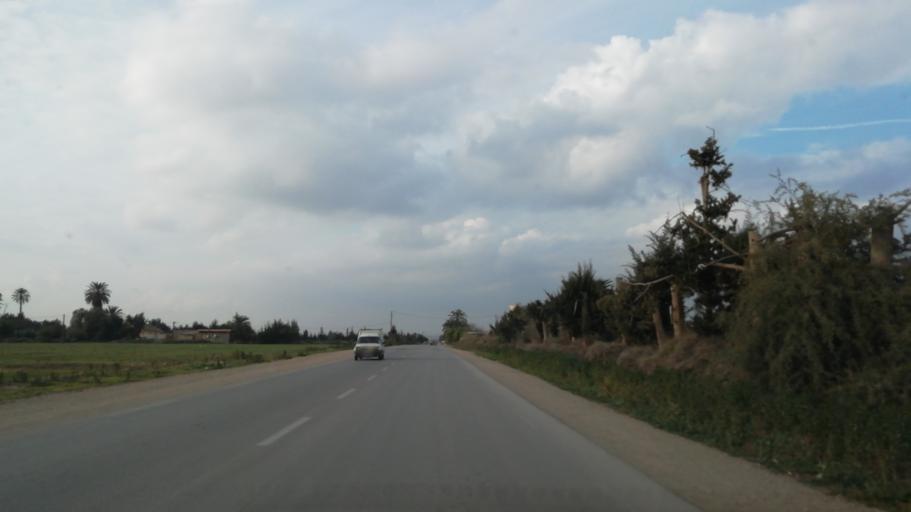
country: DZ
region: Mascara
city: Sig
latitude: 35.6859
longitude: -0.0143
